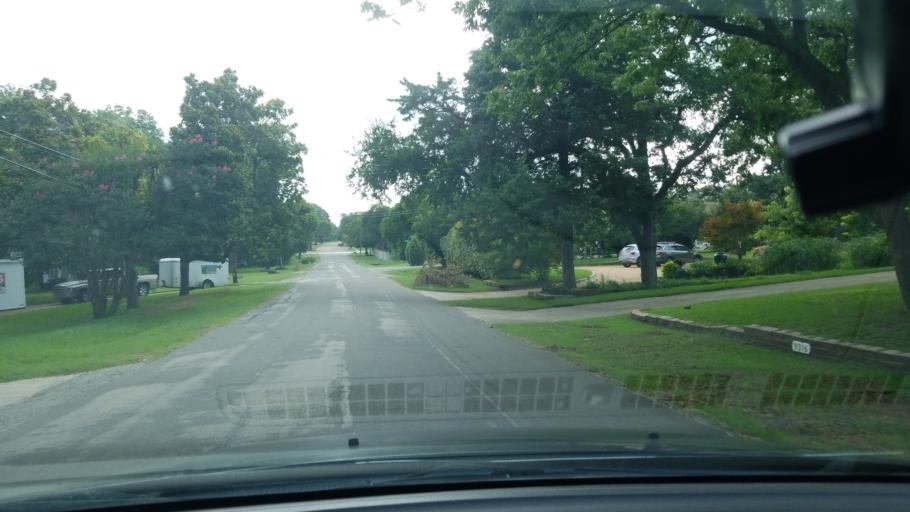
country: US
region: Texas
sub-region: Dallas County
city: Highland Park
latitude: 32.8178
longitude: -96.6926
